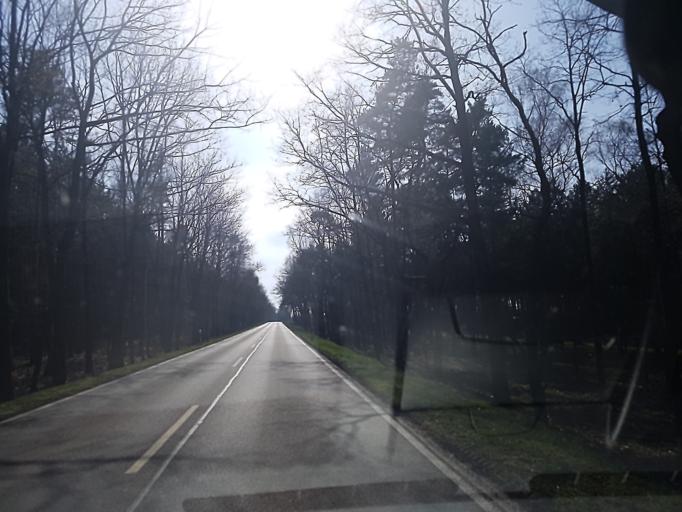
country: DE
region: Brandenburg
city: Calau
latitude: 51.7535
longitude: 13.9691
